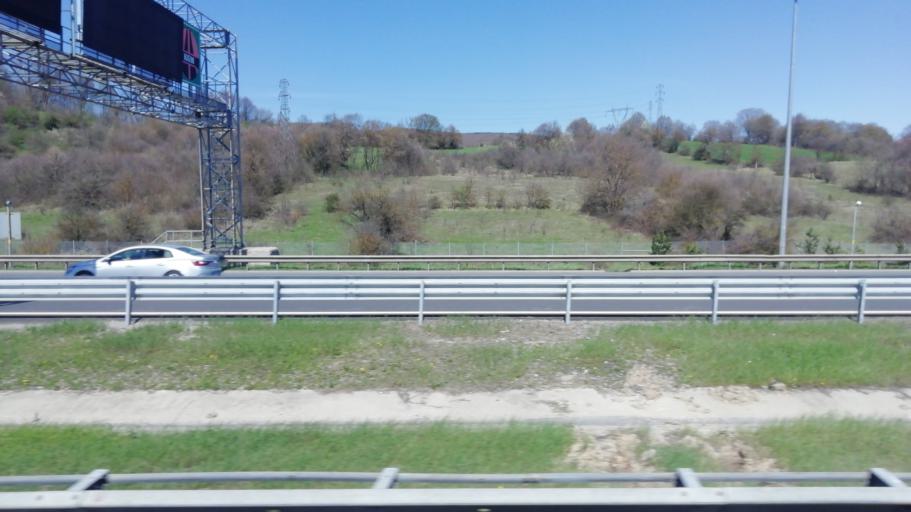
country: TR
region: Duzce
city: Kaynasli
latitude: 40.7259
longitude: 31.4463
